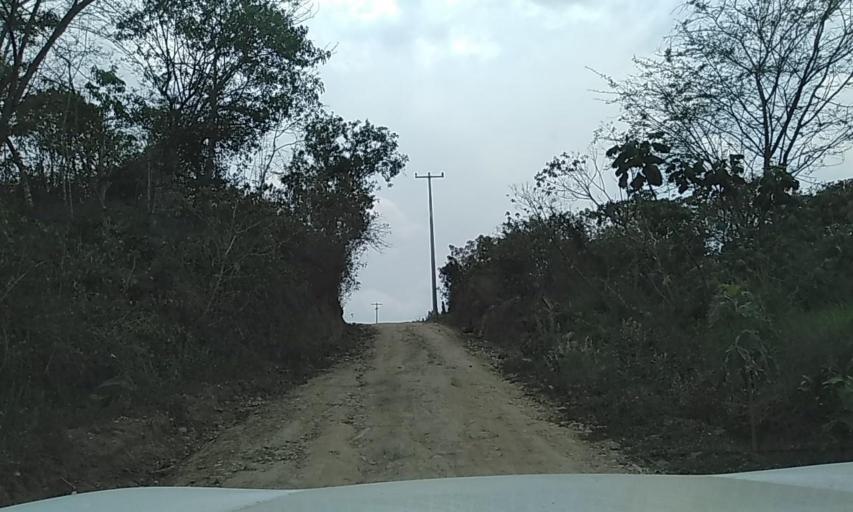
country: MX
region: Veracruz
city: El Castillo
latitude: 19.5401
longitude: -96.8766
